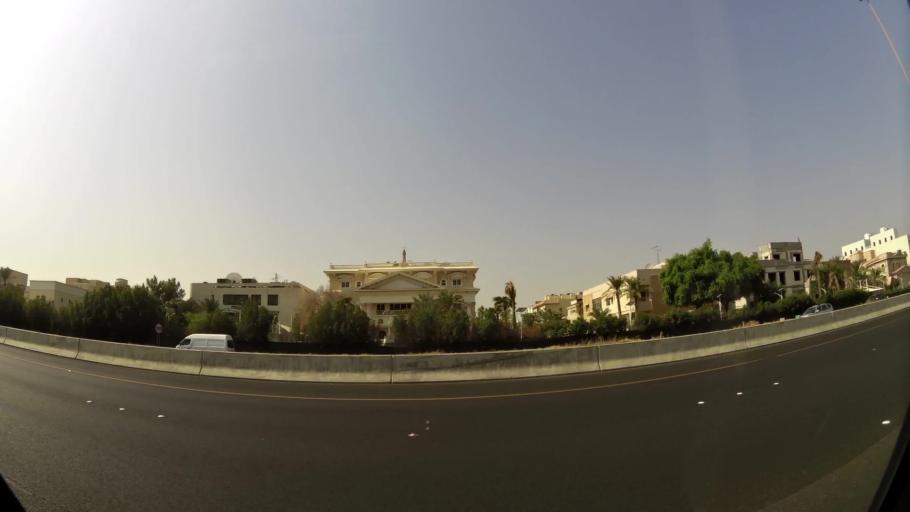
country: KW
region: Al Asimah
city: Ad Dasmah
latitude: 29.3476
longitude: 47.9962
